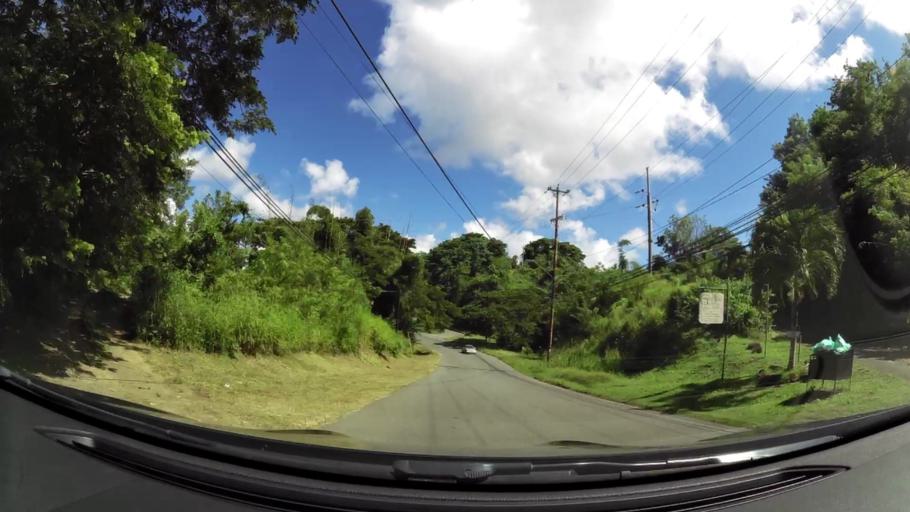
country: TT
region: Tobago
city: Scarborough
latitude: 11.2004
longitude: -60.7875
